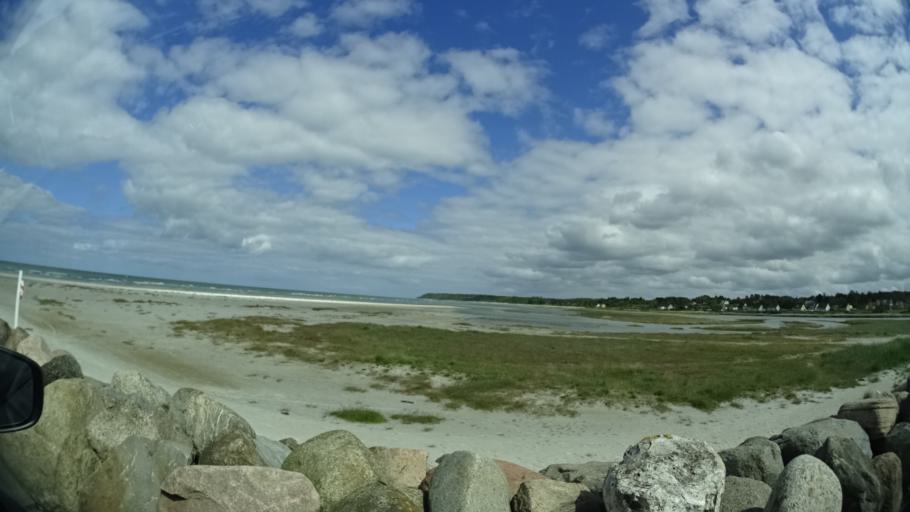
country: DK
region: Central Jutland
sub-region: Norddjurs Kommune
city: Grenaa
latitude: 56.5342
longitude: 10.7145
